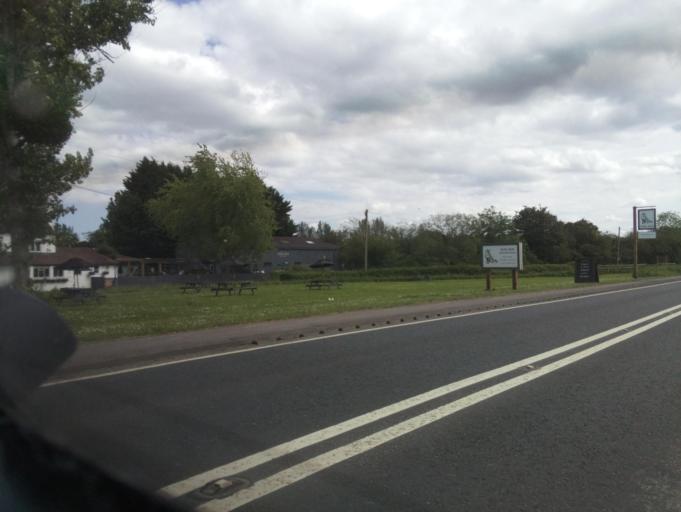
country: GB
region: England
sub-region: Worcestershire
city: Bransford
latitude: 52.1761
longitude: -2.2884
